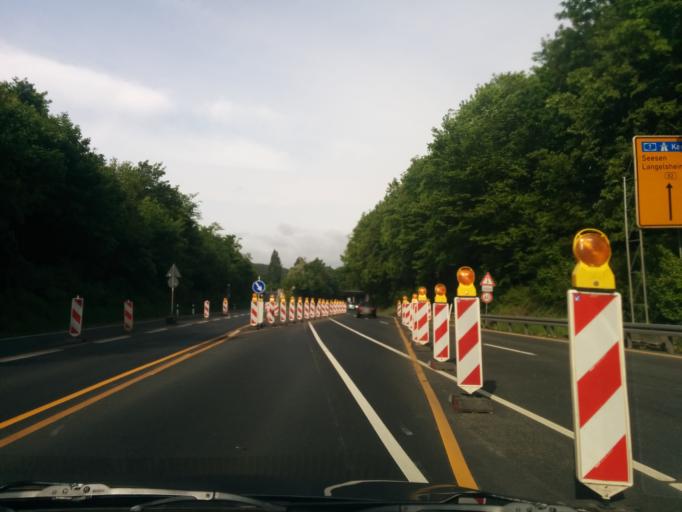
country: DE
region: Lower Saxony
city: Goslar
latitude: 51.9203
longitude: 10.4189
